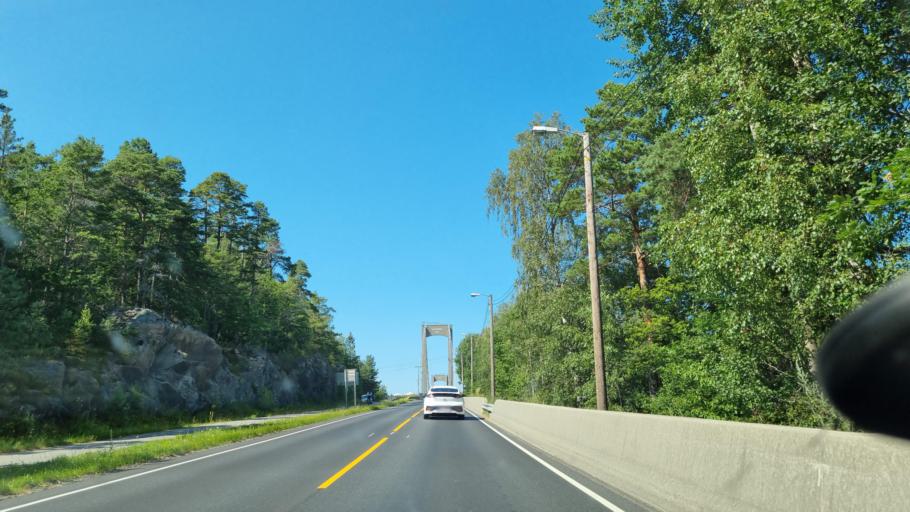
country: NO
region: Aust-Agder
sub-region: Arendal
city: Arendal
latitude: 58.4677
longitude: 8.8248
